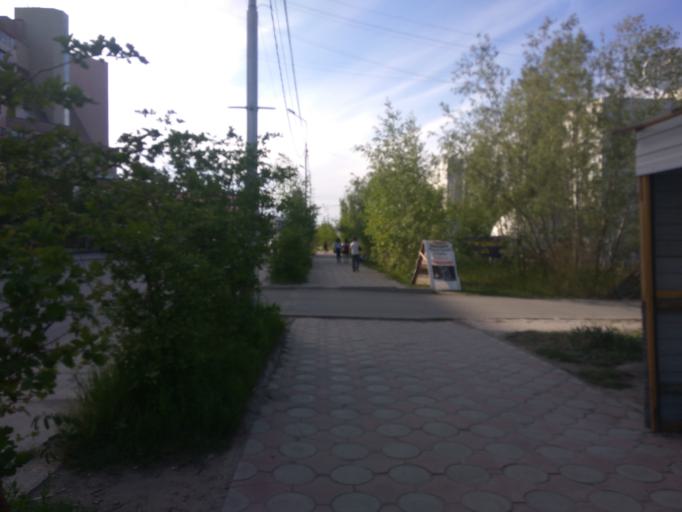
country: RU
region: Sakha
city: Yakutsk
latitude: 62.0248
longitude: 129.7350
